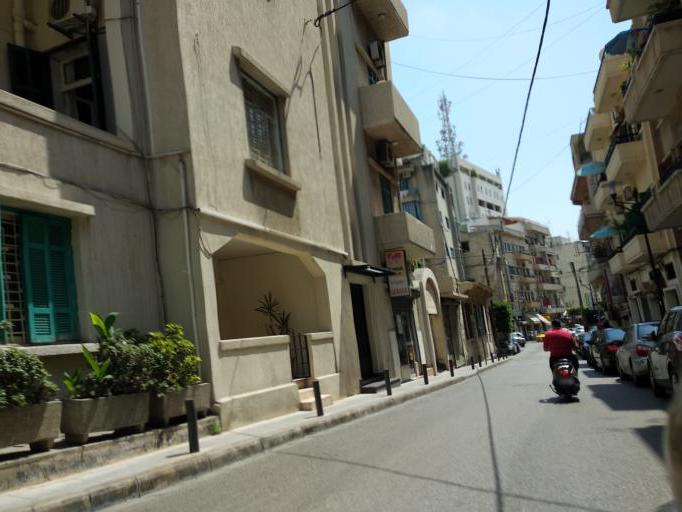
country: LB
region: Beyrouth
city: Beirut
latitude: 33.8919
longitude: 35.5283
